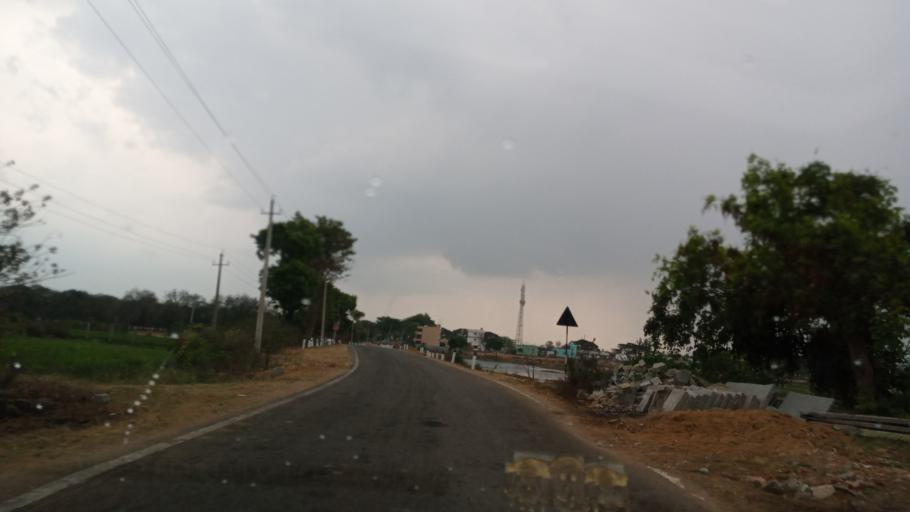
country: IN
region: Karnataka
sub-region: Kolar
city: Mulbagal
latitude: 13.1123
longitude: 78.3355
